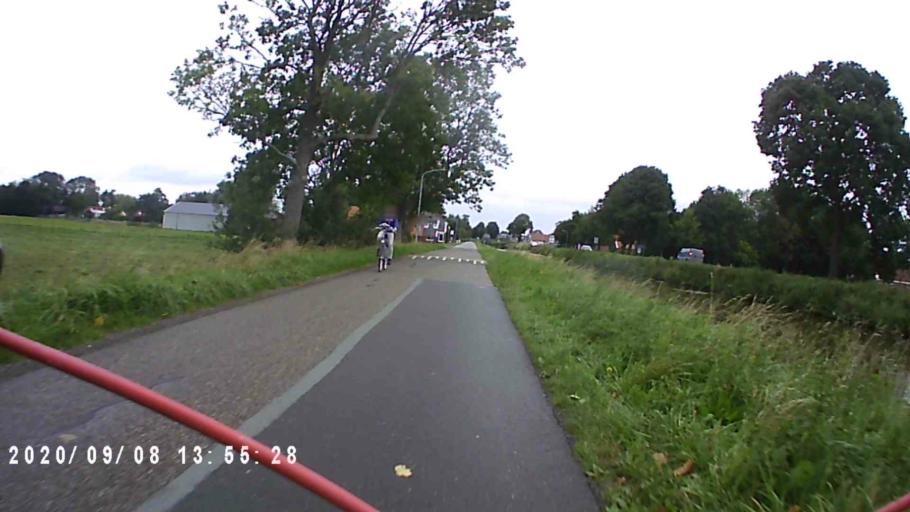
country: NL
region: Groningen
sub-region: Gemeente Veendam
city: Veendam
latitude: 53.1564
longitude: 6.8636
